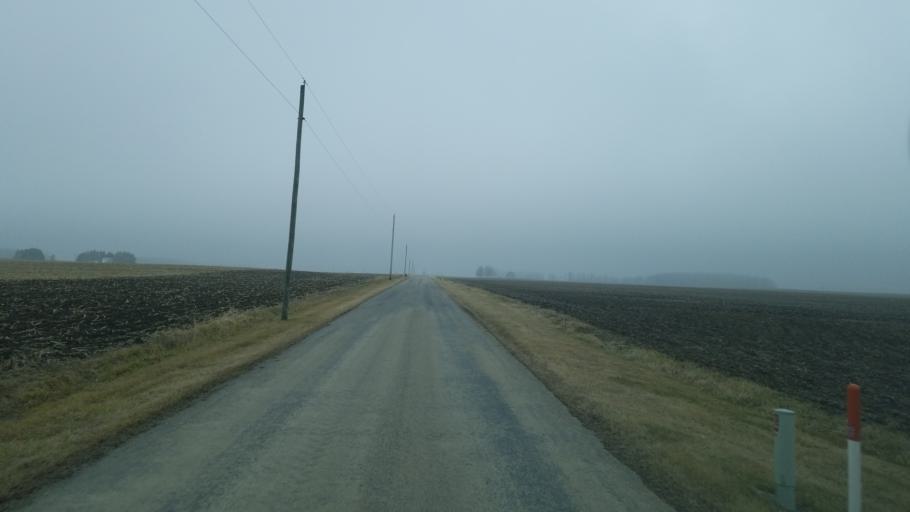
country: US
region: Indiana
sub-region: Wells County
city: Bluffton
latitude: 40.6044
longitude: -85.1071
